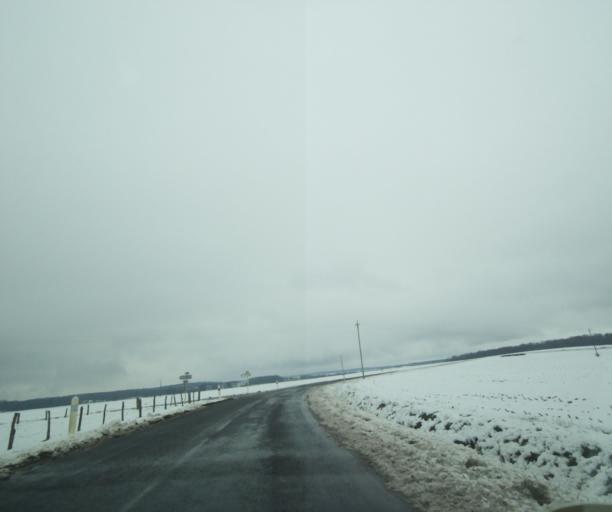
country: FR
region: Champagne-Ardenne
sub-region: Departement de la Haute-Marne
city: Montier-en-Der
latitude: 48.4383
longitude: 4.8070
